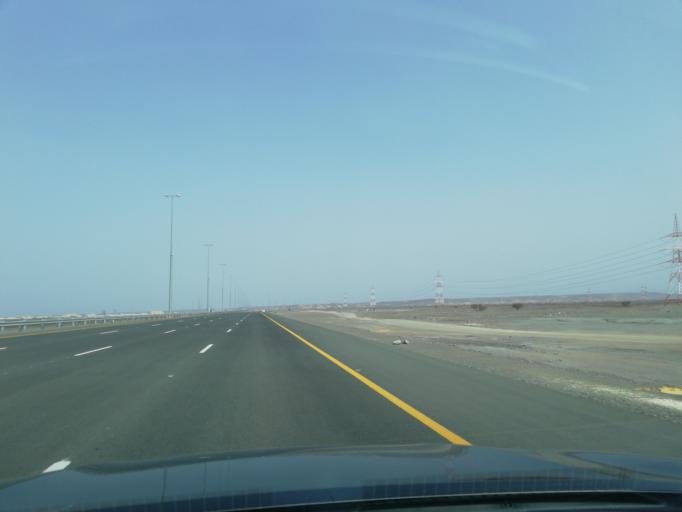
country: OM
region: Al Batinah
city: Al Sohar
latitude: 24.3204
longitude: 56.5732
